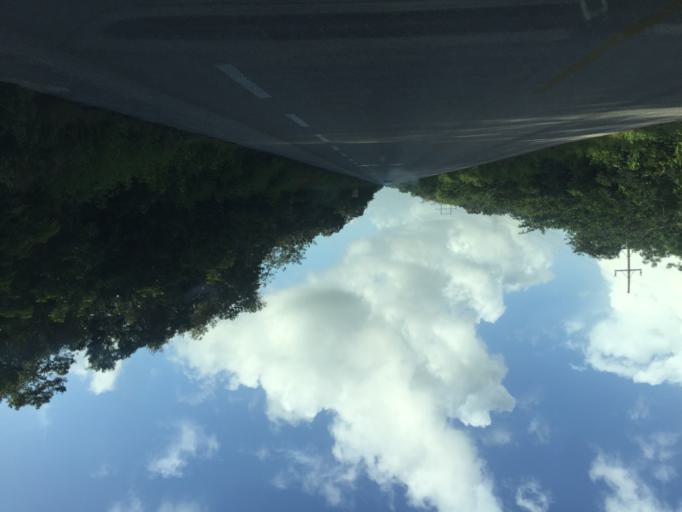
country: MX
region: Quintana Roo
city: Coba
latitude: 20.4754
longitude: -87.6908
